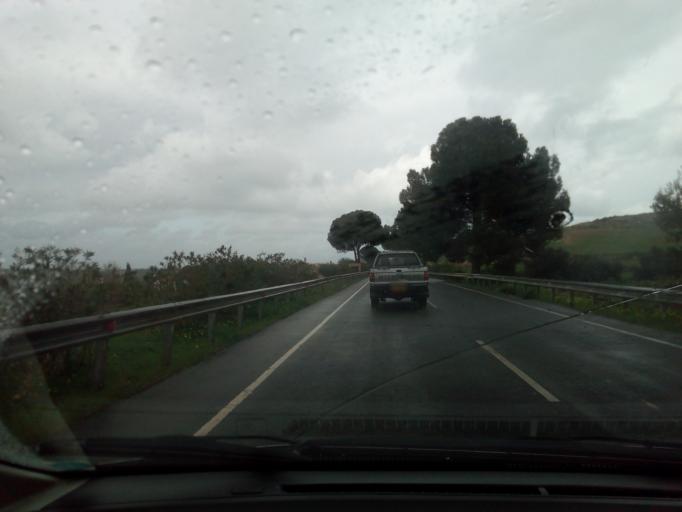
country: CY
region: Pafos
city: Polis
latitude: 35.0139
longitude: 32.4356
